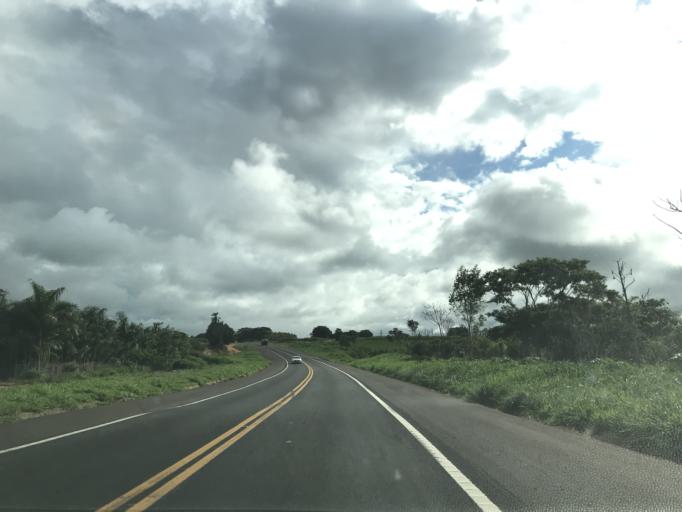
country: BR
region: Sao Paulo
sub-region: Penapolis
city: Penapolis
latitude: -21.4839
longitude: -50.2084
